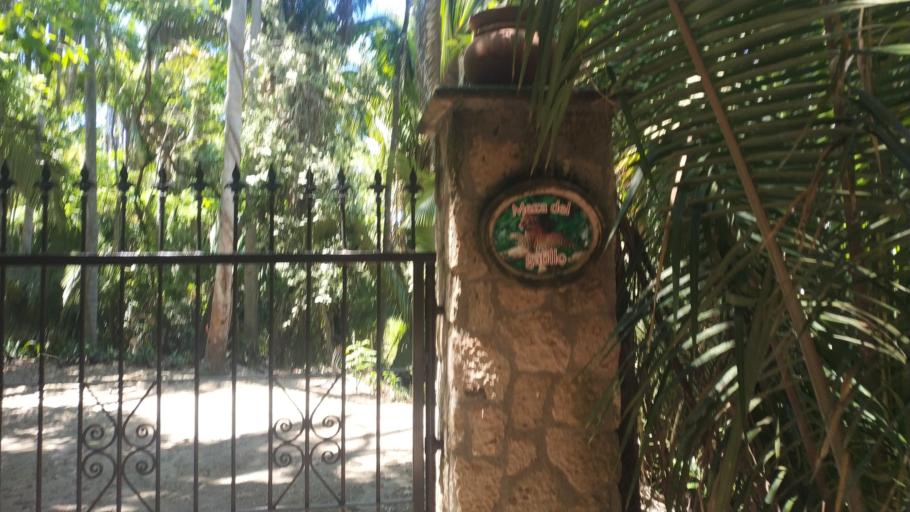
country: MX
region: Nayarit
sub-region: Bahia de Banderas
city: Lo de Marcos
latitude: 20.9224
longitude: -105.4034
